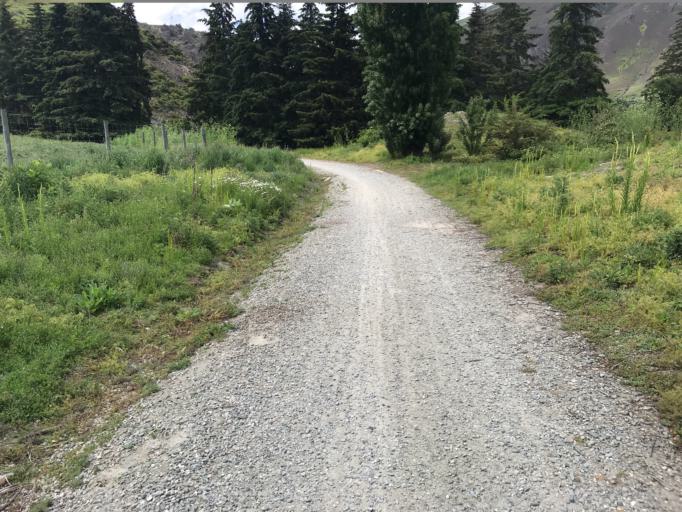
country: NZ
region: Otago
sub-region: Queenstown-Lakes District
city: Arrowtown
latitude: -45.0029
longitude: 168.8773
